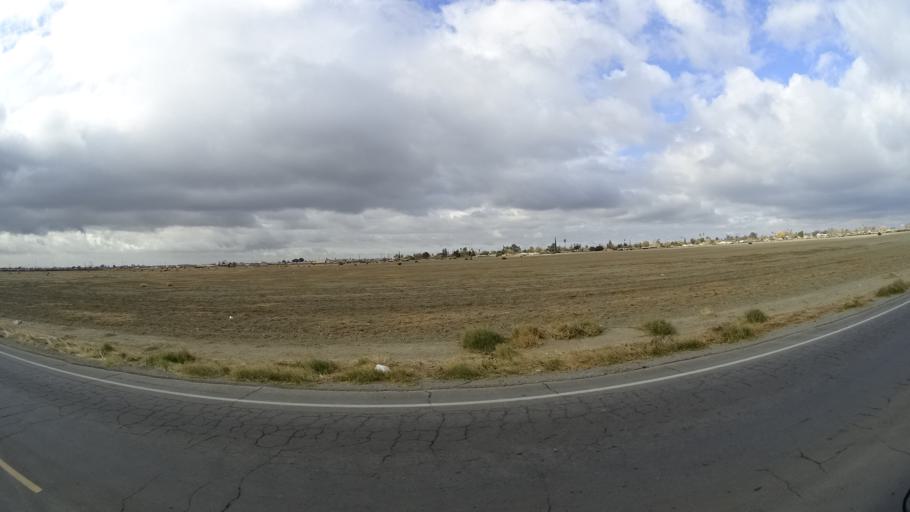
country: US
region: California
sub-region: Kern County
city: Greenfield
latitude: 35.3001
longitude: -118.9853
